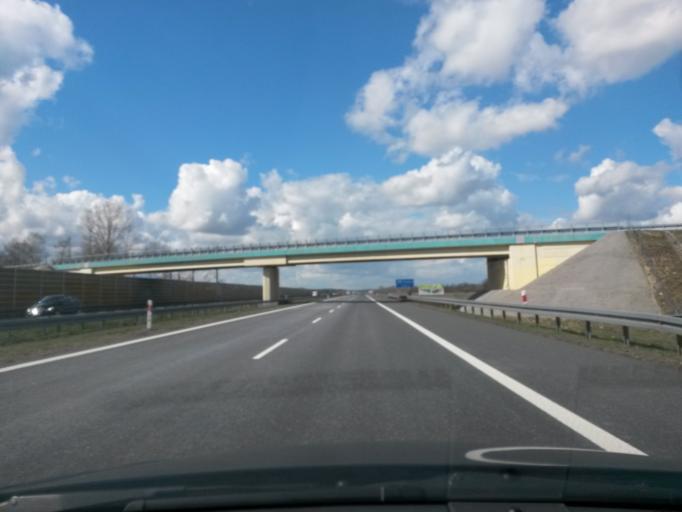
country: PL
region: Greater Poland Voivodeship
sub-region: Powiat kolski
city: Dabie
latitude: 52.0479
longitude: 18.8522
